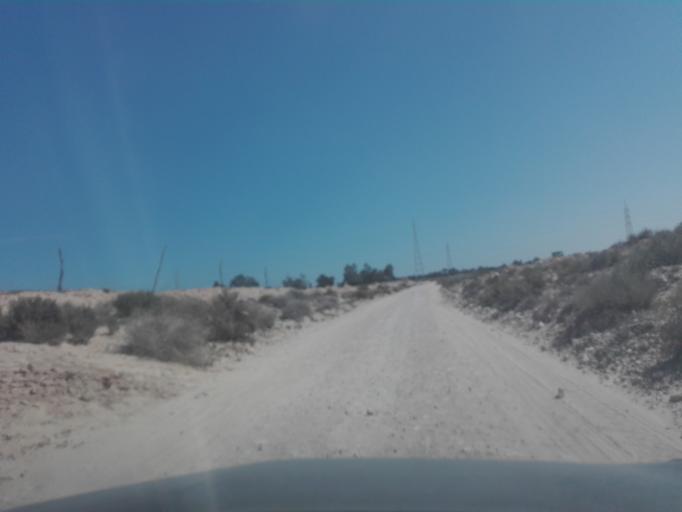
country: TN
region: Qabis
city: Gabes
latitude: 33.8750
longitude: 10.0269
